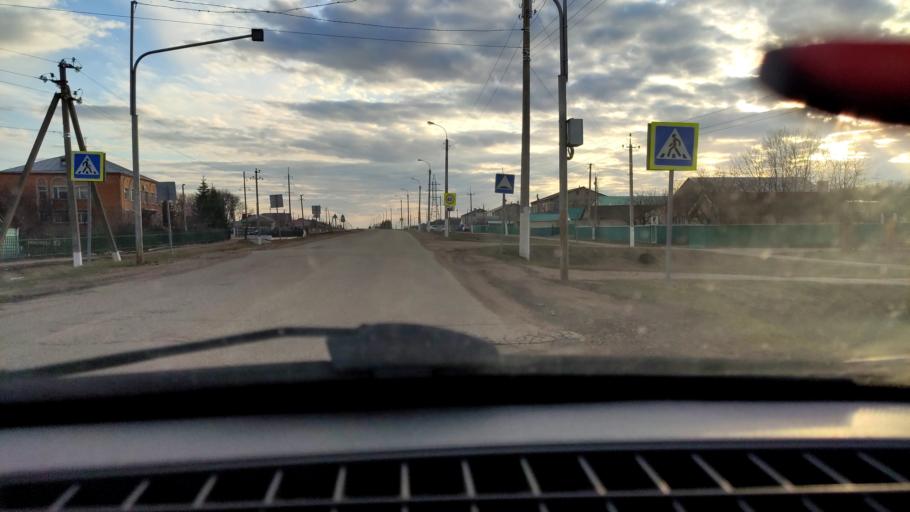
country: RU
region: Bashkortostan
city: Tolbazy
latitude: 54.0082
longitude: 55.8773
